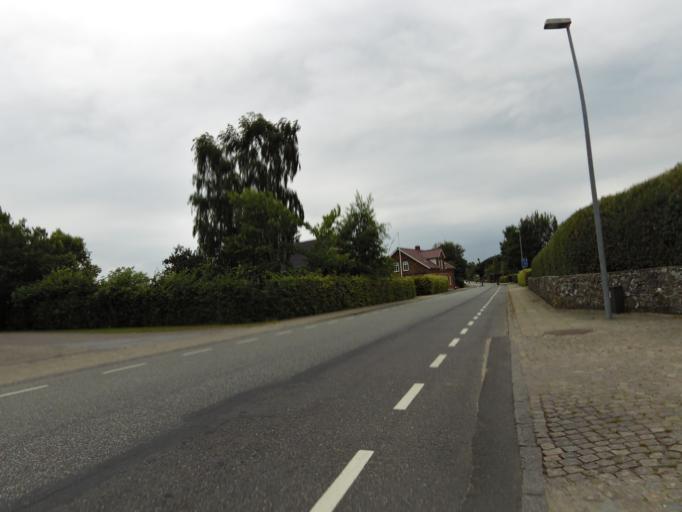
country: DK
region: South Denmark
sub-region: Tonder Kommune
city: Logumkloster
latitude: 55.0762
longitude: 8.9302
